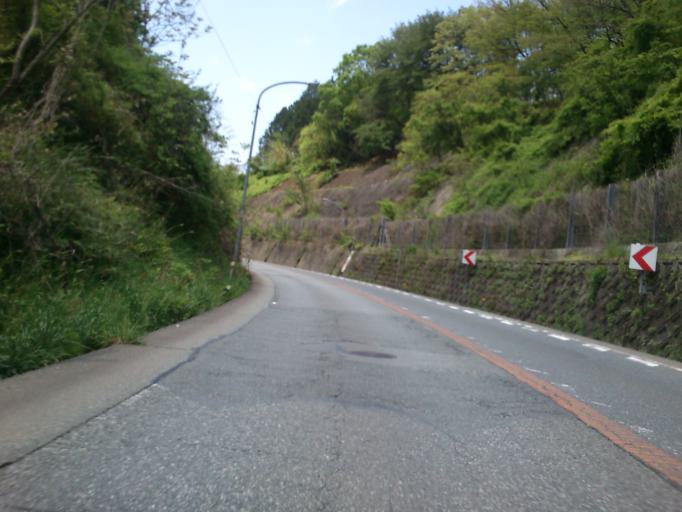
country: JP
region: Kyoto
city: Fukuchiyama
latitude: 35.3306
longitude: 134.9410
